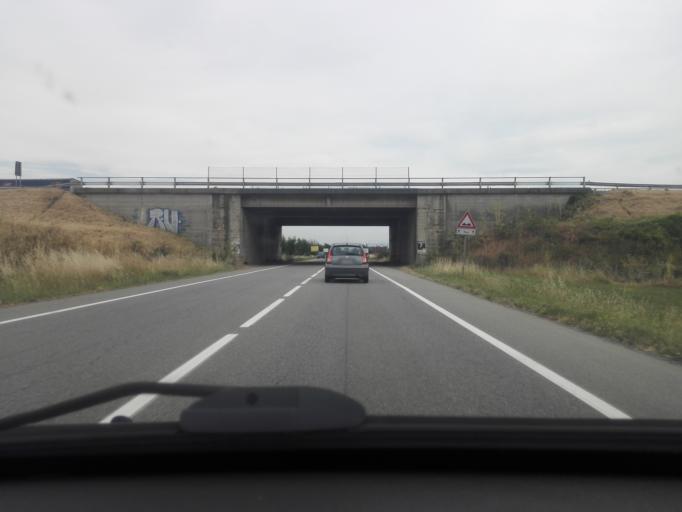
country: IT
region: Piedmont
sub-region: Provincia di Alessandria
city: Pozzolo Formigaro
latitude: 44.8101
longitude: 8.7652
